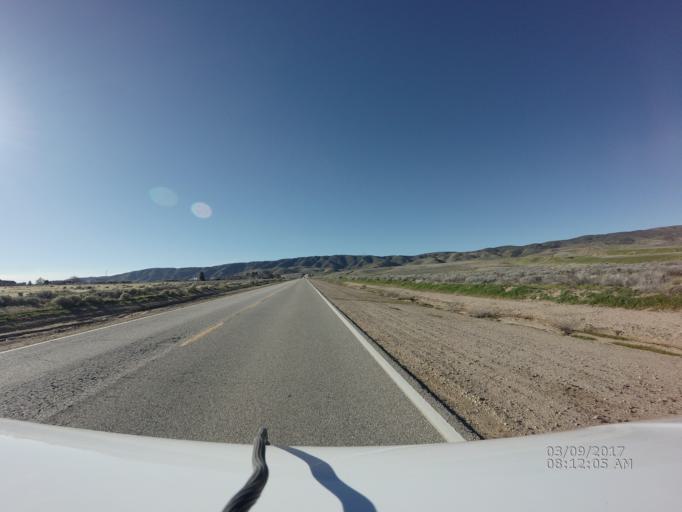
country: US
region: California
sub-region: Los Angeles County
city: Leona Valley
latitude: 34.6794
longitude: -118.3242
